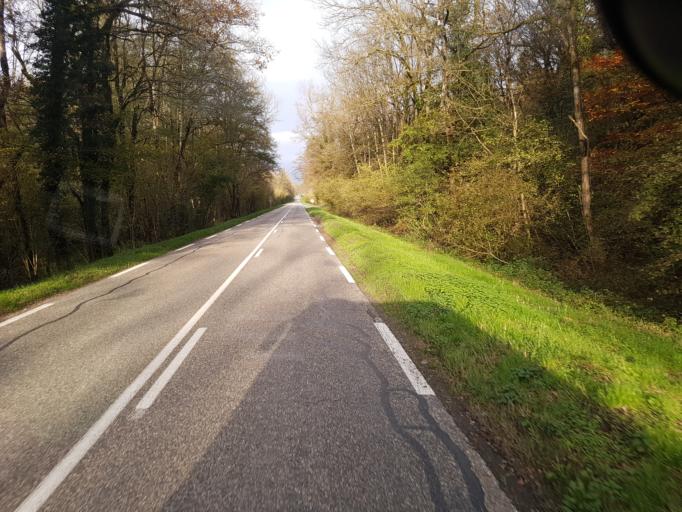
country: FR
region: Rhone-Alpes
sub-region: Departement de la Haute-Savoie
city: Frangy
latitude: 45.9959
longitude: 5.8518
